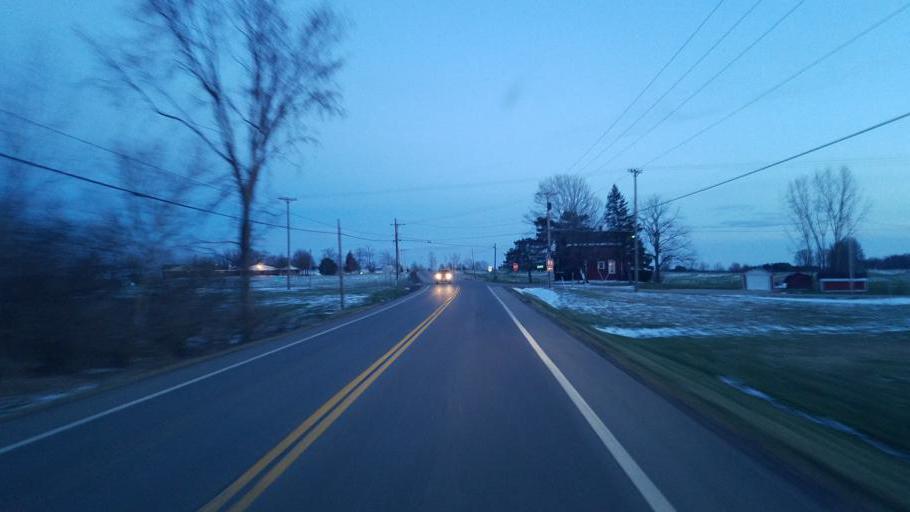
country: US
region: Ohio
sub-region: Ashland County
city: Ashland
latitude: 40.8066
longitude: -82.2717
